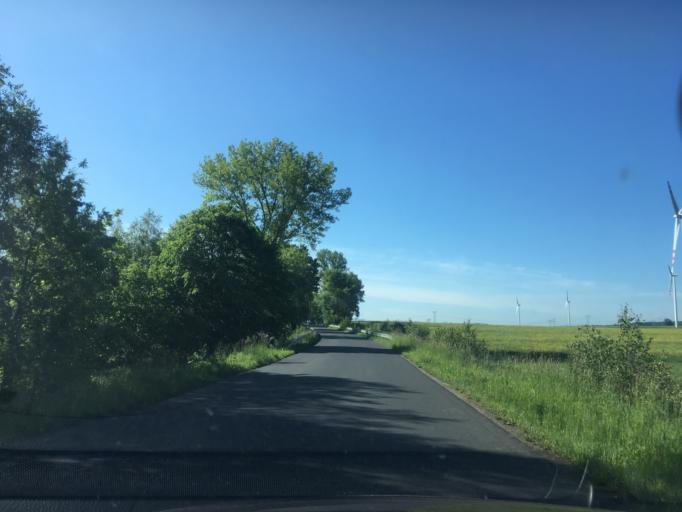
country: PL
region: Lower Silesian Voivodeship
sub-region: Powiat zgorzelecki
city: Sulikow
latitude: 51.0976
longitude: 15.0398
